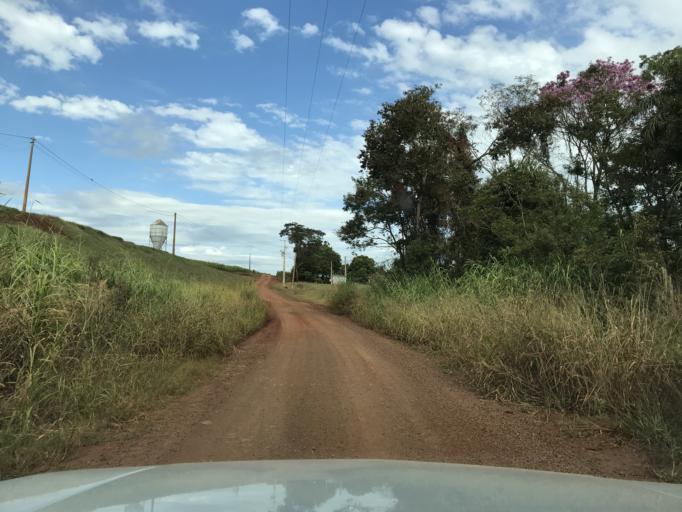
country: BR
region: Parana
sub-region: Palotina
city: Palotina
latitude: -24.3242
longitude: -53.8056
